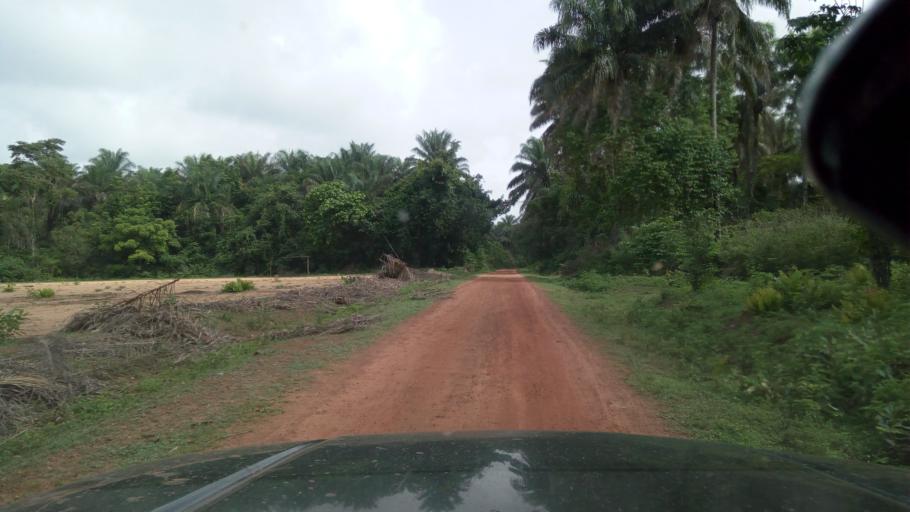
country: SL
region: Northern Province
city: Mange
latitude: 8.8104
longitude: -12.9289
